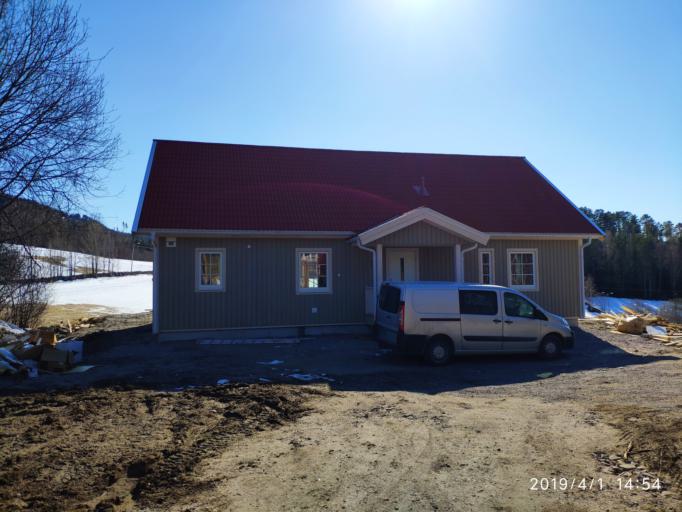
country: NO
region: Telemark
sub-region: Nissedal
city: Treungen
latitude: 59.1601
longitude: 8.5322
